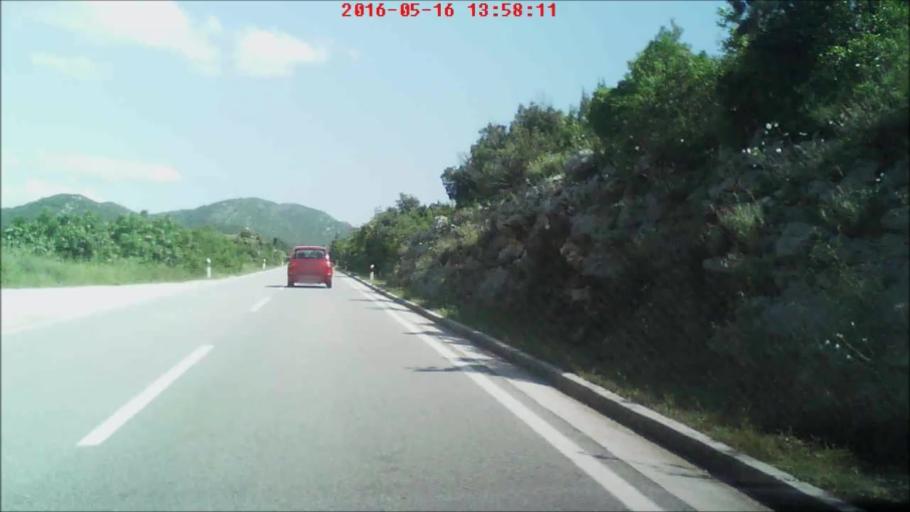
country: HR
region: Dubrovacko-Neretvanska
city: Ston
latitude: 42.8412
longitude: 17.7139
